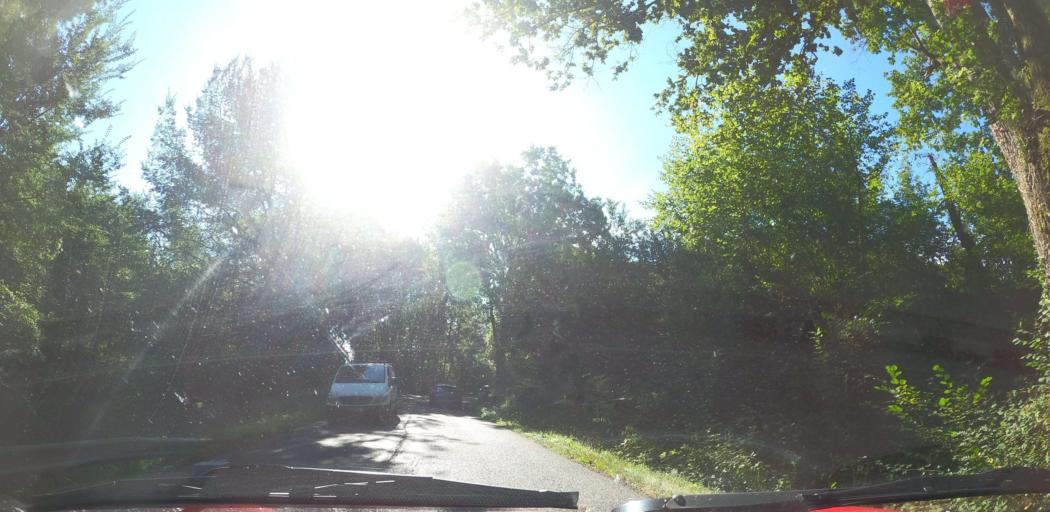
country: FR
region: Aquitaine
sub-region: Departement des Pyrenees-Atlantiques
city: Saint-Pee-sur-Nivelle
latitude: 43.3697
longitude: -1.5461
